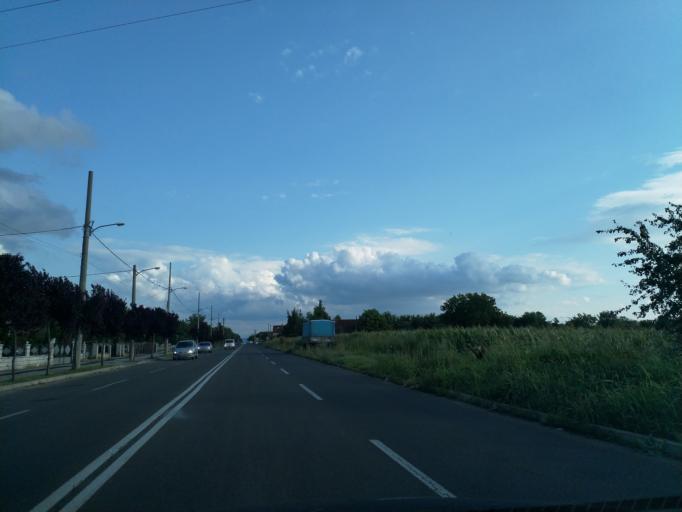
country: RS
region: Central Serbia
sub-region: Pomoravski Okrug
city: Paracin
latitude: 43.8359
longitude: 21.4159
